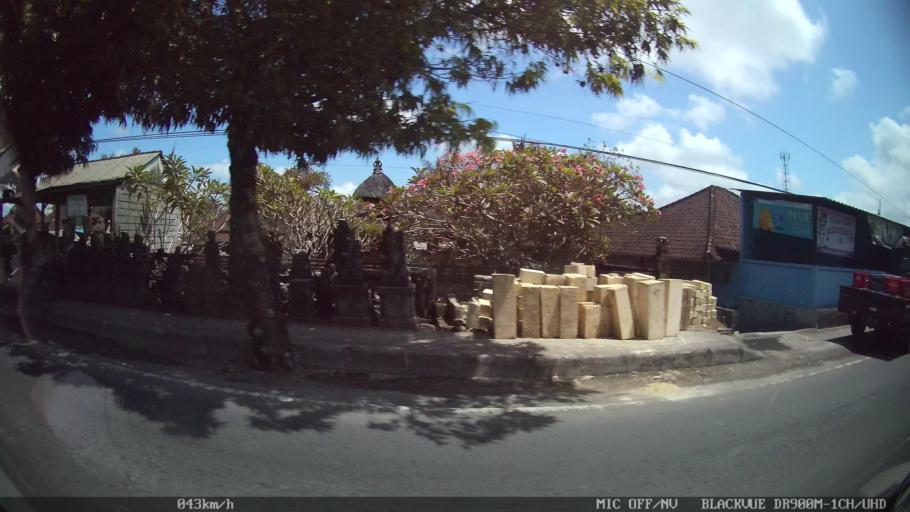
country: ID
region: Bali
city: Banjar Jabejero
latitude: -8.5995
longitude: 115.2533
